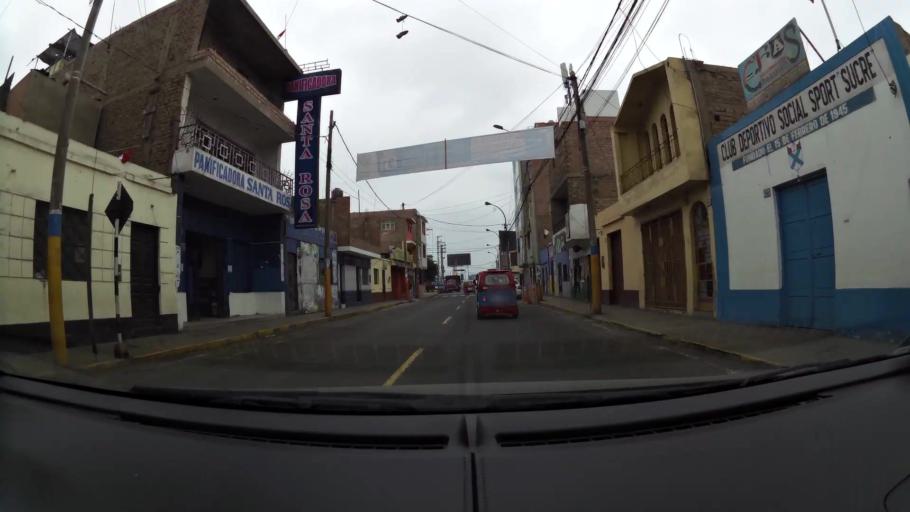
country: PE
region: Lima
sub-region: Barranca
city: Barranca
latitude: -10.7558
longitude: -77.7571
